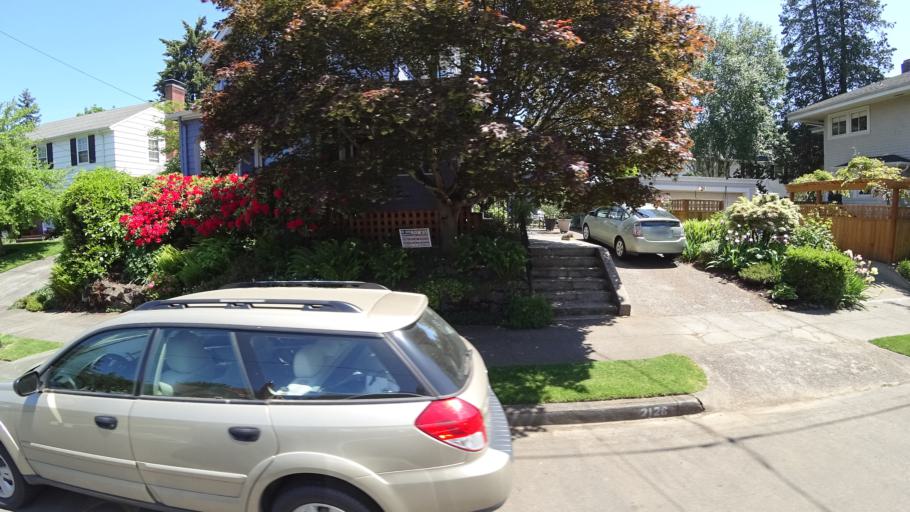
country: US
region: Oregon
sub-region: Multnomah County
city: Portland
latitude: 45.5378
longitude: -122.6391
